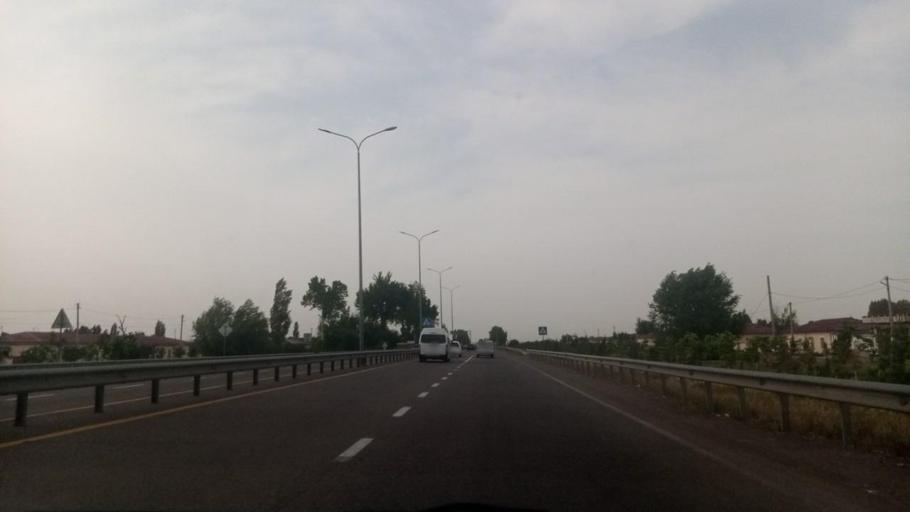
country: UZ
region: Toshkent
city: Tuytepa
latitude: 41.1324
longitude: 69.4358
